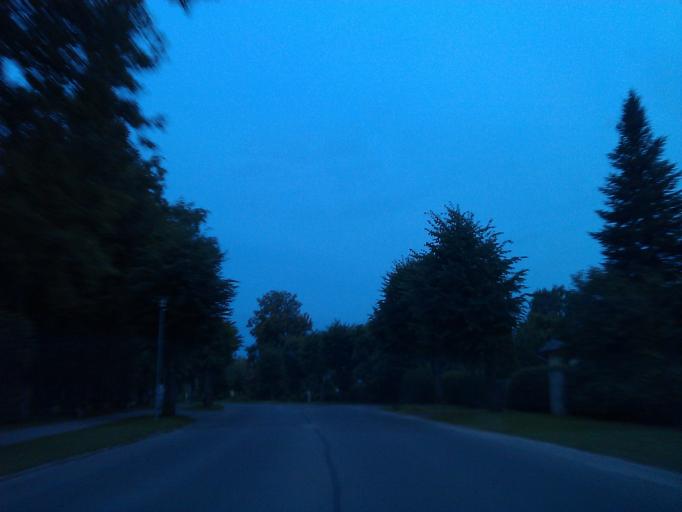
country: LV
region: Sigulda
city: Sigulda
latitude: 57.1452
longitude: 24.8441
